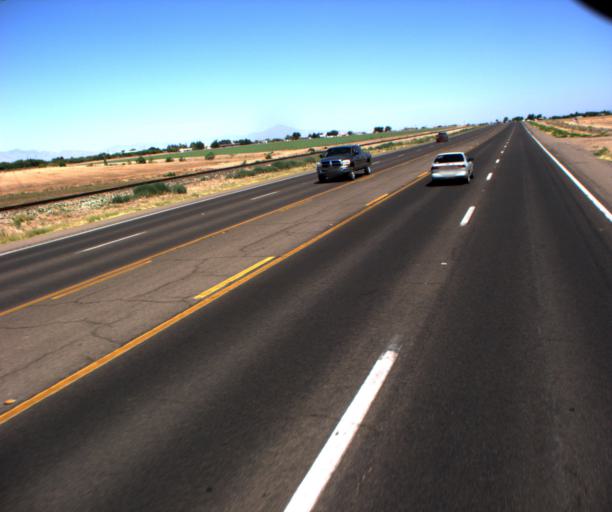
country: US
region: Arizona
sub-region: Graham County
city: Pima
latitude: 32.8779
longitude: -109.8038
